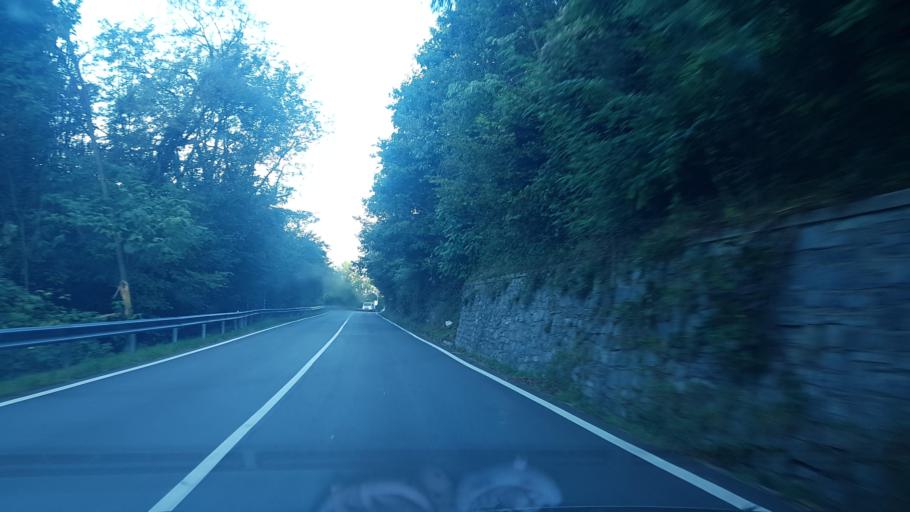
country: IT
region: Piedmont
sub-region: Provincia Verbano-Cusio-Ossola
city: Vignone
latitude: 45.9629
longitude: 8.5676
